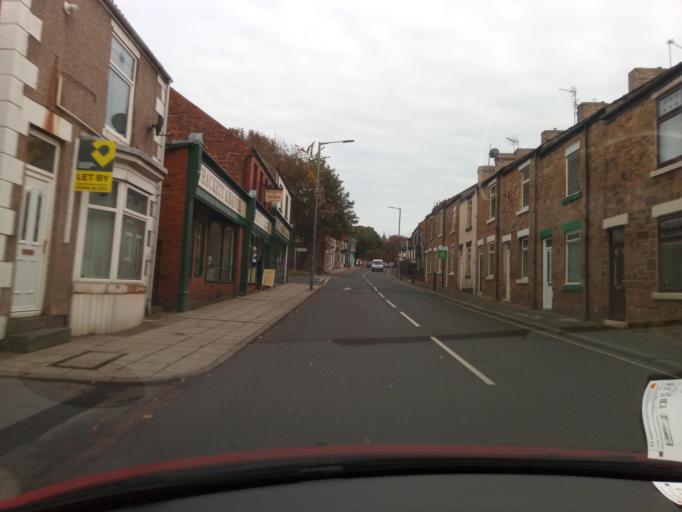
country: GB
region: England
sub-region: County Durham
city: Shildon
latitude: 54.6325
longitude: -1.6518
